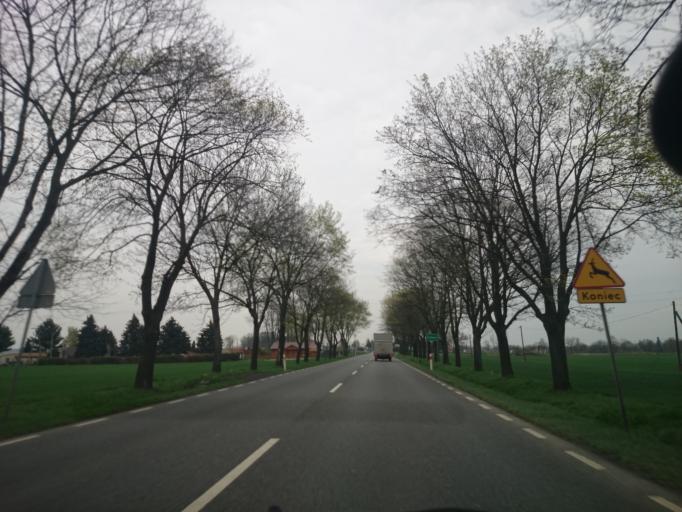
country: PL
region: Opole Voivodeship
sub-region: Powiat nyski
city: Otmuchow
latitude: 50.4473
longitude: 17.1023
